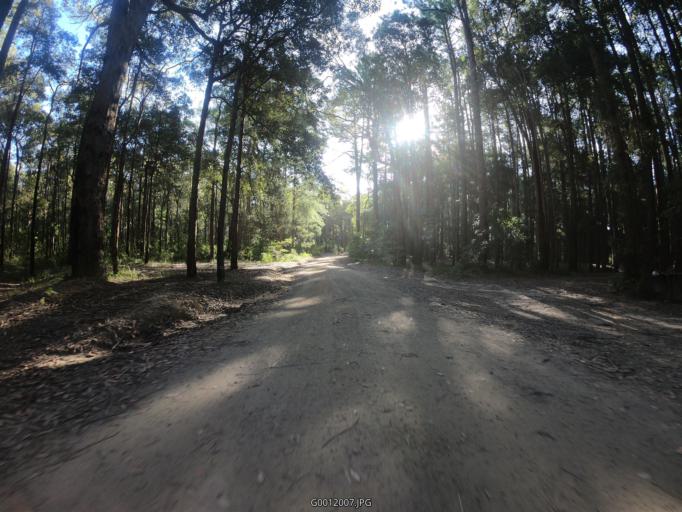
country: AU
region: New South Wales
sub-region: Lake Macquarie Shire
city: Cooranbong
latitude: -33.0665
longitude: 151.3373
